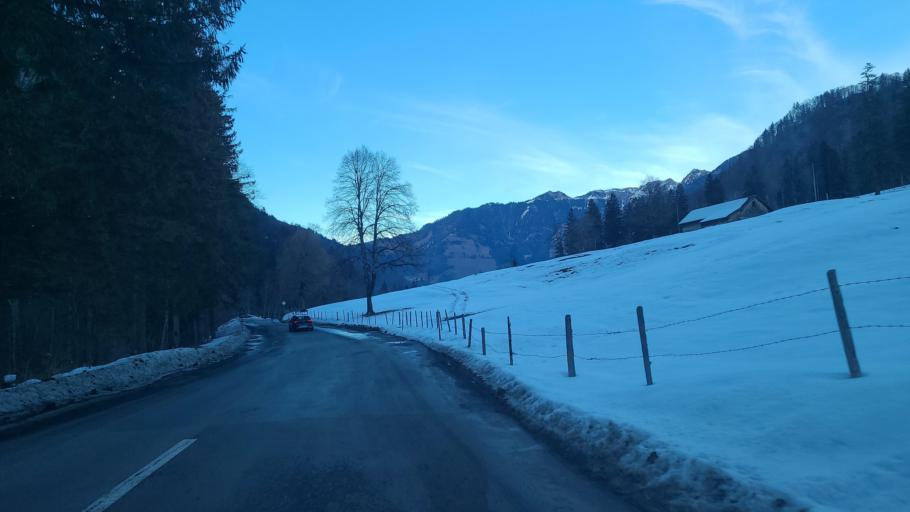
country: CH
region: Obwalden
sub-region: Obwalden
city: Sachseln
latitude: 46.8191
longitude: 8.2836
